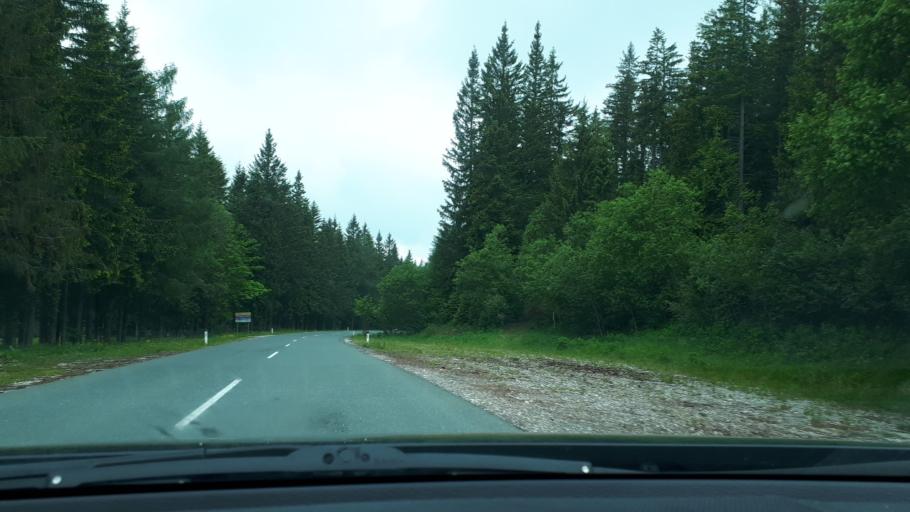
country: AT
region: Styria
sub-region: Politischer Bezirk Voitsberg
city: Modriach
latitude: 46.9299
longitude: 15.0058
